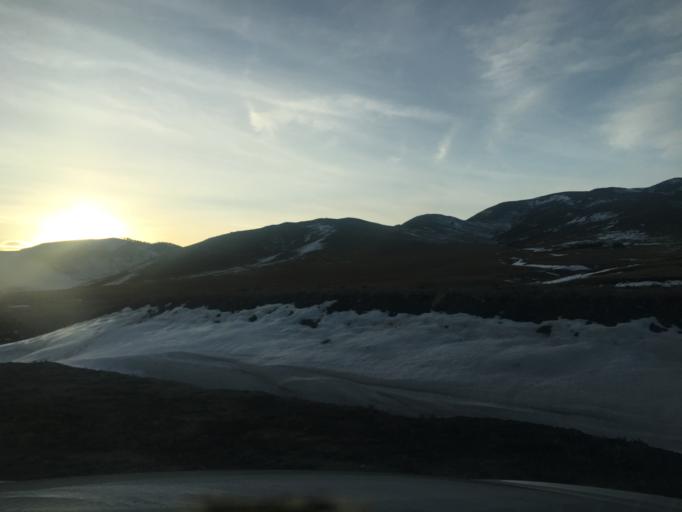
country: MN
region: Central Aimak
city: Mandal
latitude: 48.2336
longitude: 106.7217
